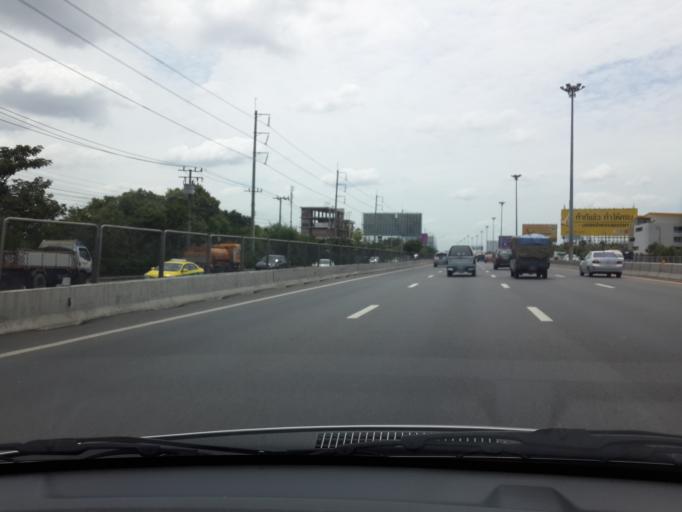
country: TH
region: Bangkok
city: Suan Luang
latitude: 13.7362
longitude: 100.6723
